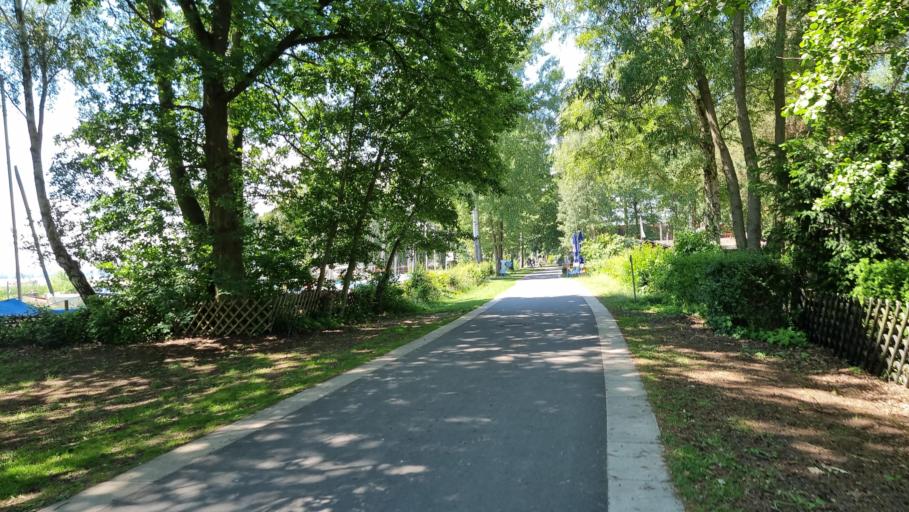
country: DE
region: Lower Saxony
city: Hagenburg
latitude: 52.4888
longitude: 9.3142
